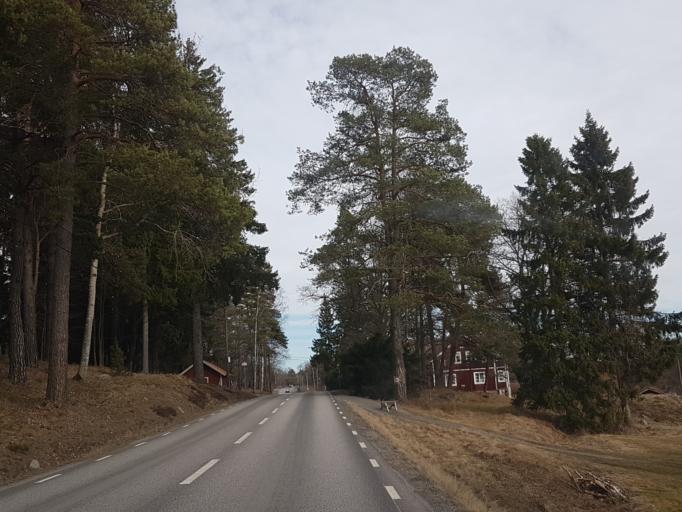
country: SE
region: Stockholm
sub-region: Norrtalje Kommun
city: Norrtalje
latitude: 59.6791
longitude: 18.7347
